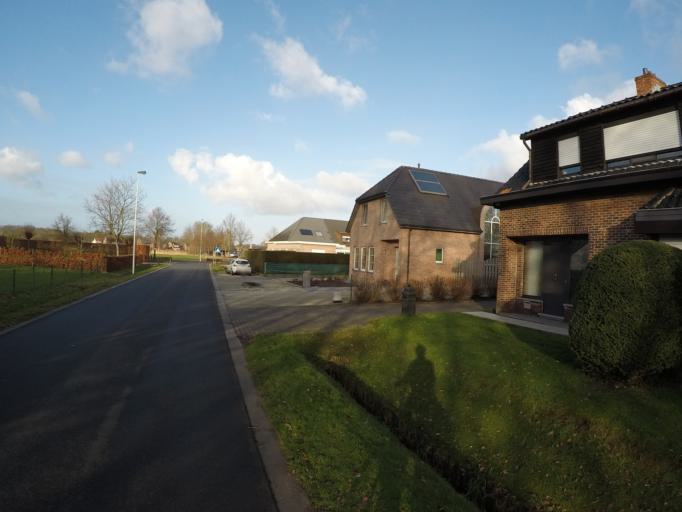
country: BE
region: Flanders
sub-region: Provincie Antwerpen
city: Lier
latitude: 51.1447
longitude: 4.6164
